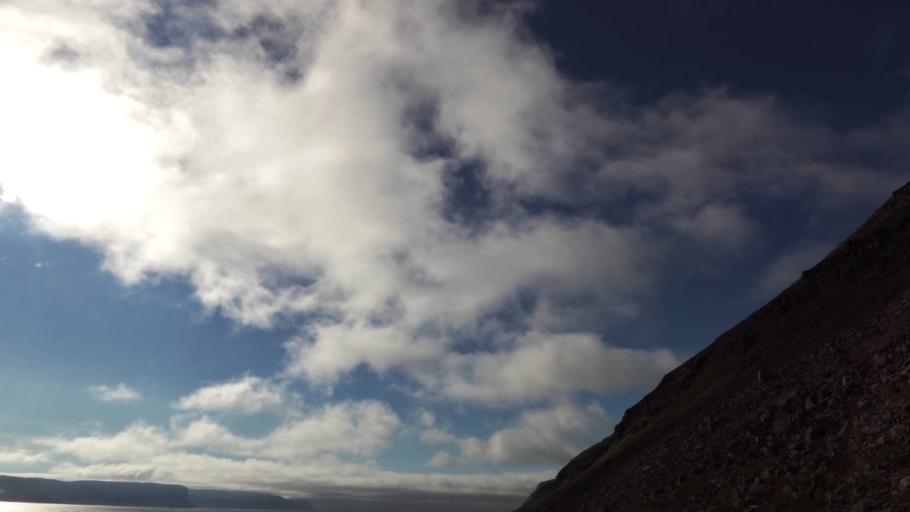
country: IS
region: West
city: Olafsvik
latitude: 65.5631
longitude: -23.9148
